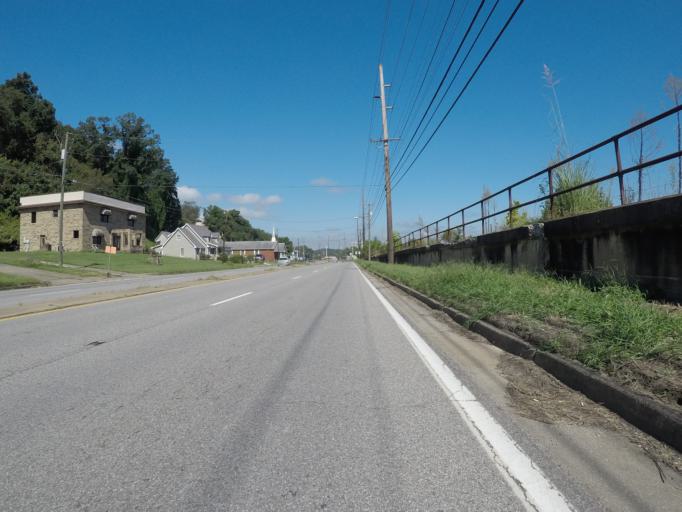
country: US
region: Ohio
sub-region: Lawrence County
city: South Point
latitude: 38.4307
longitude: -82.6037
